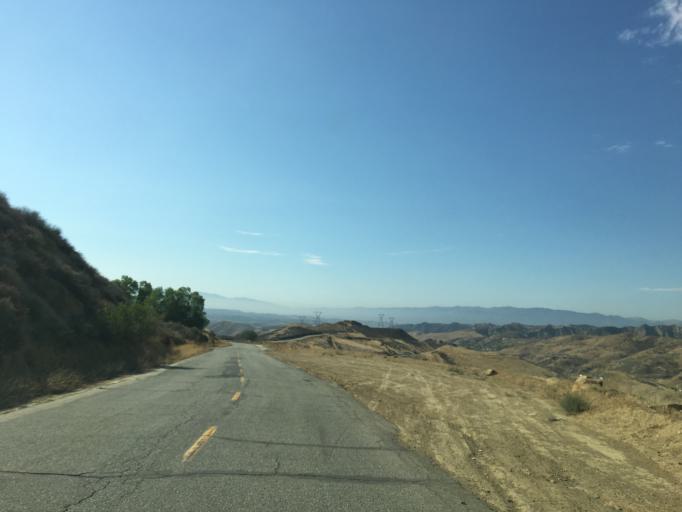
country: US
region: California
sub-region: Los Angeles County
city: Castaic
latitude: 34.5388
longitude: -118.6475
